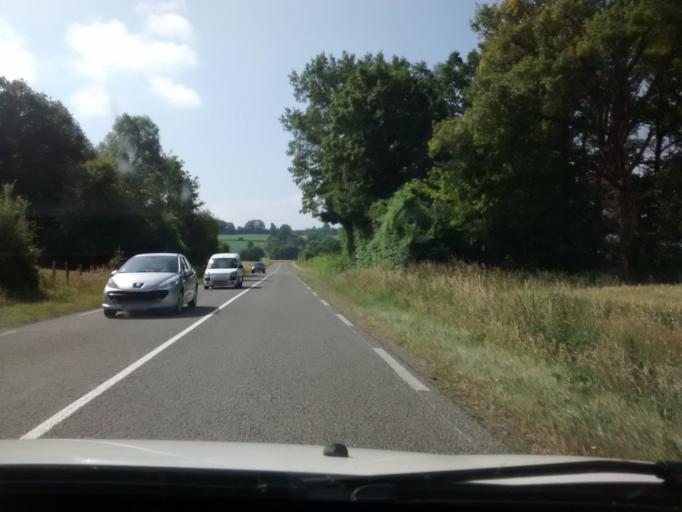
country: FR
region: Pays de la Loire
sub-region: Departement de la Sarthe
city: Cherre
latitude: 48.1285
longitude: 0.7012
